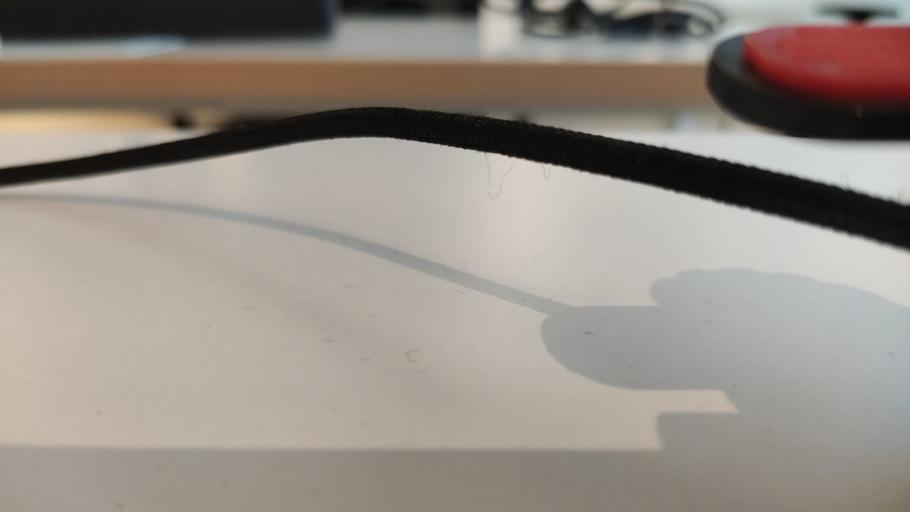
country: RU
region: Moskovskaya
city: Novopetrovskoye
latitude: 55.9379
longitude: 36.4352
